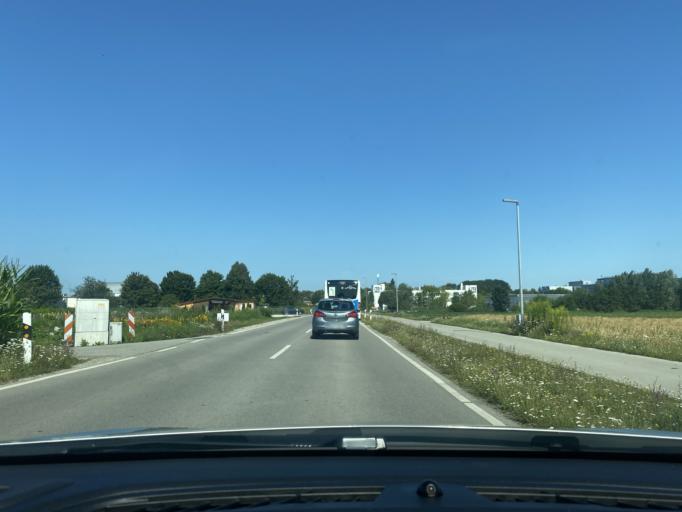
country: DE
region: Bavaria
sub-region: Upper Bavaria
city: Worth
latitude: 48.2727
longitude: 11.8996
